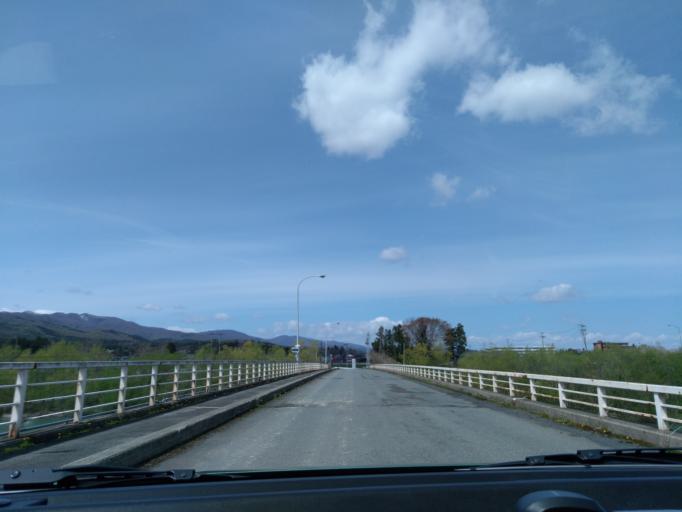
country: JP
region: Iwate
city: Kitakami
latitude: 39.3019
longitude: 140.9760
